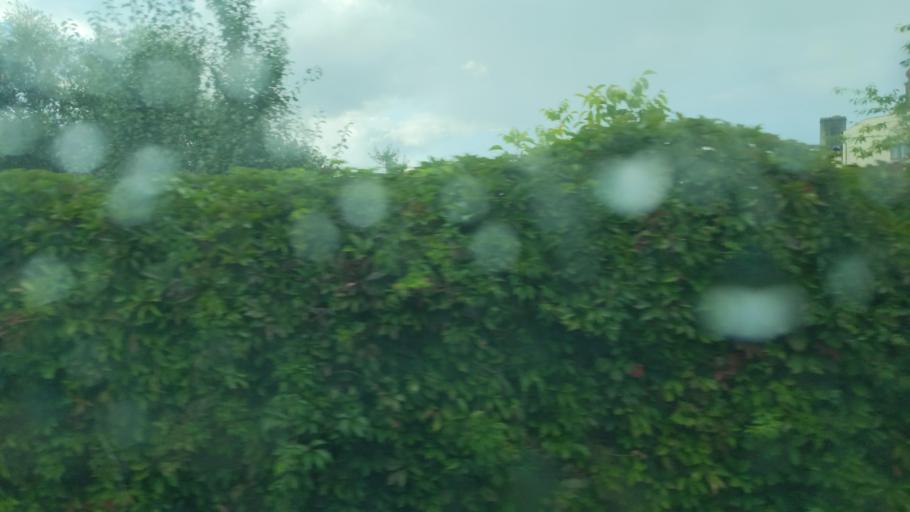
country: CZ
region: Central Bohemia
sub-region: Okres Nymburk
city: Sadska
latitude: 50.1325
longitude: 14.9681
